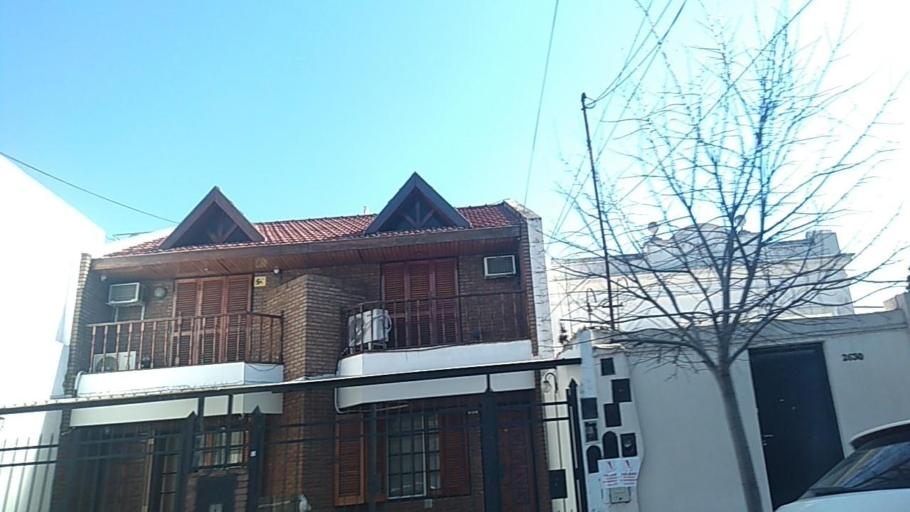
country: AR
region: Buenos Aires F.D.
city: Villa Santa Rita
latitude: -34.6083
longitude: -58.4993
